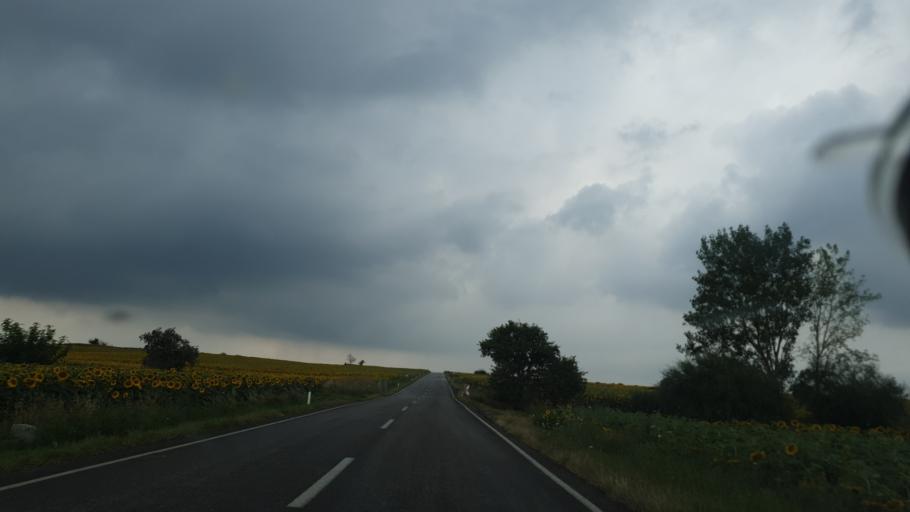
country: TR
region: Kirklareli
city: Pehlivankoy
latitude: 41.2177
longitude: 26.9656
